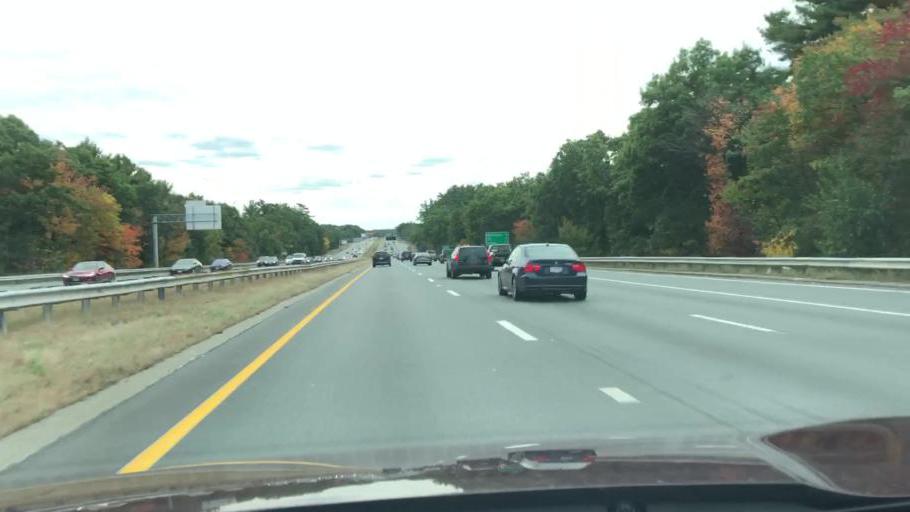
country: US
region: Massachusetts
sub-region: Essex County
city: Andover
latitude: 42.6168
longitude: -71.1756
